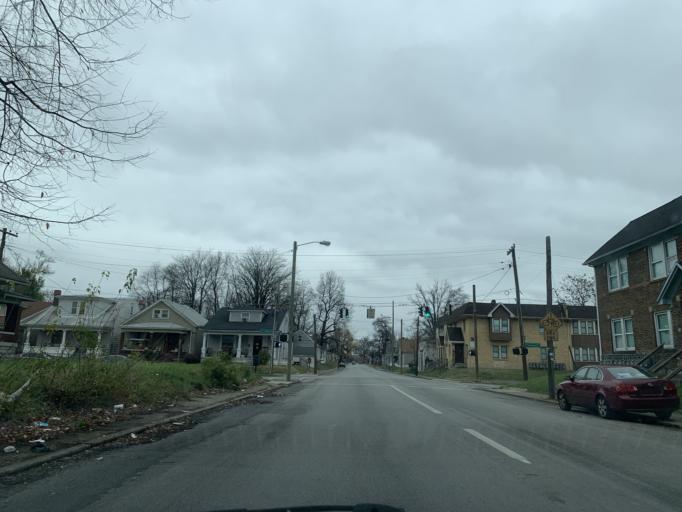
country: US
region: Kentucky
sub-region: Jefferson County
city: Louisville
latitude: 38.2407
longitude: -85.7881
